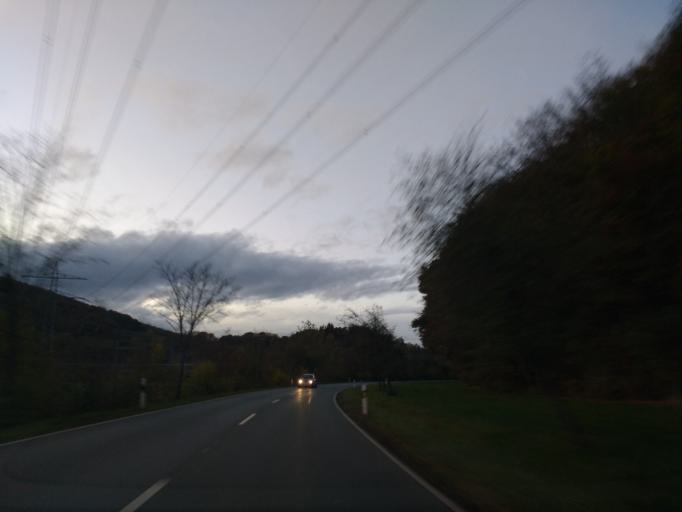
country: DE
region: Hesse
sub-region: Regierungsbezirk Kassel
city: Waldeck
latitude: 51.1655
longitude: 9.0557
